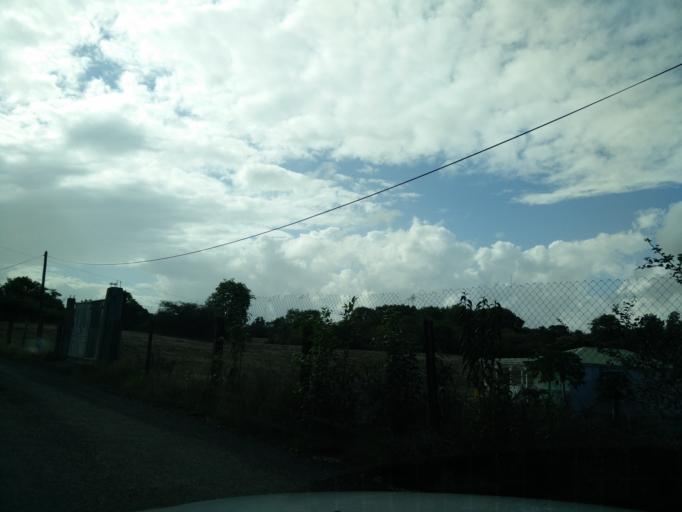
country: GP
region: Guadeloupe
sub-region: Guadeloupe
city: Sainte-Anne
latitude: 16.2483
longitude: -61.3774
